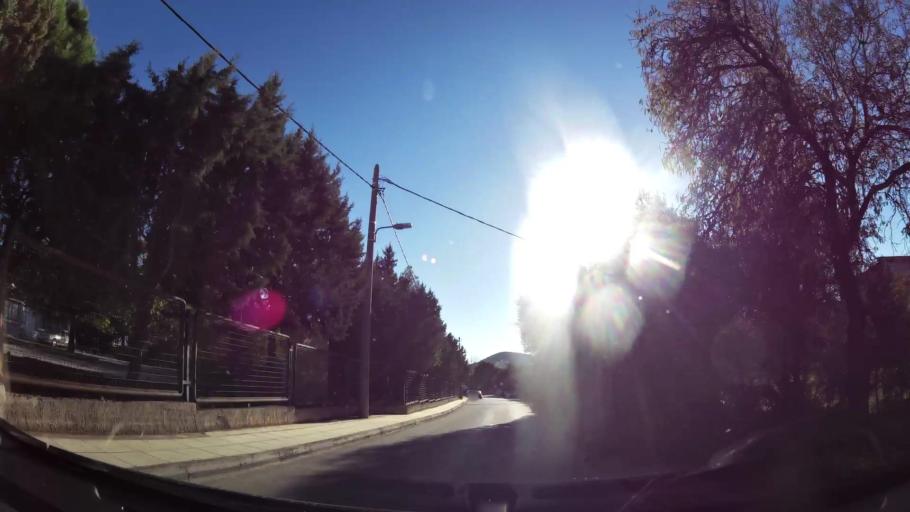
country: GR
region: Attica
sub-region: Nomarchia Anatolikis Attikis
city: Vari
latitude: 37.8323
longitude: 23.8060
